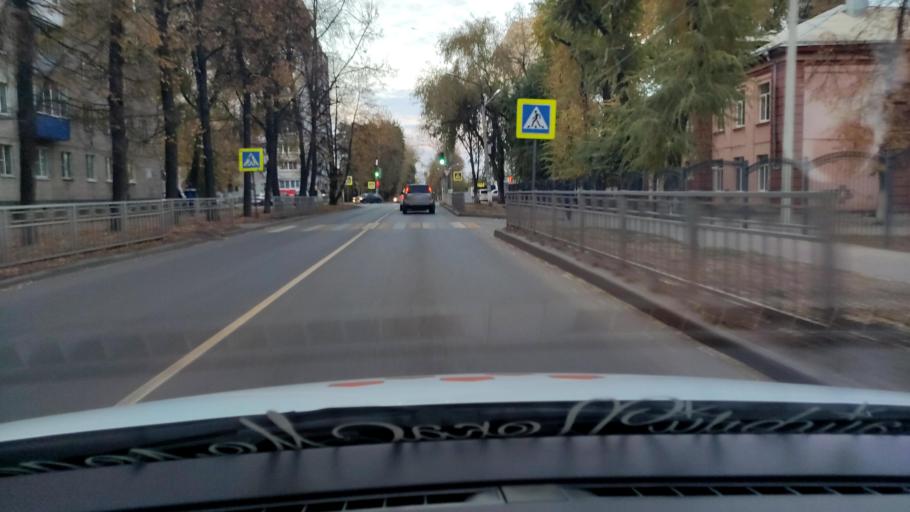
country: RU
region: Voronezj
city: Voronezh
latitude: 51.6863
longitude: 39.1909
